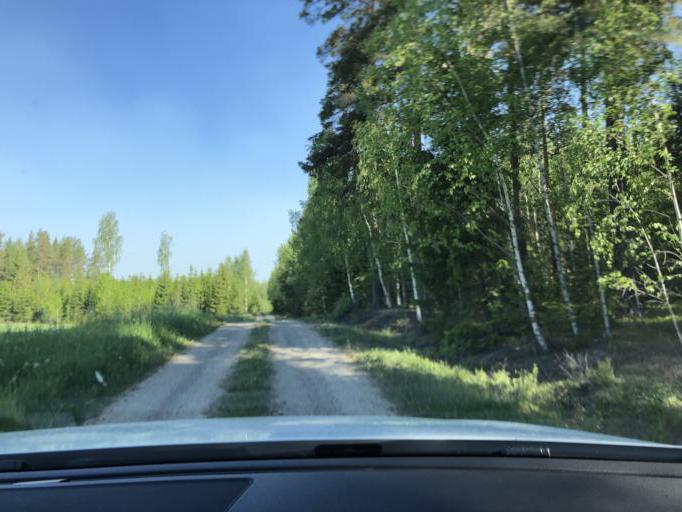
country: SE
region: Dalarna
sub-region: Avesta Kommun
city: Horndal
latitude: 60.2071
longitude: 16.4928
